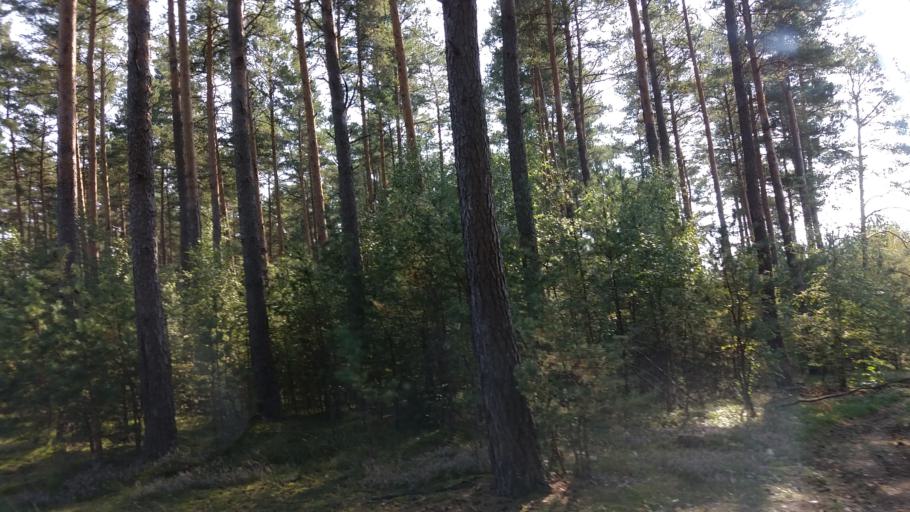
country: PL
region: West Pomeranian Voivodeship
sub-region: Powiat drawski
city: Kalisz Pomorski
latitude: 53.1300
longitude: 15.9399
